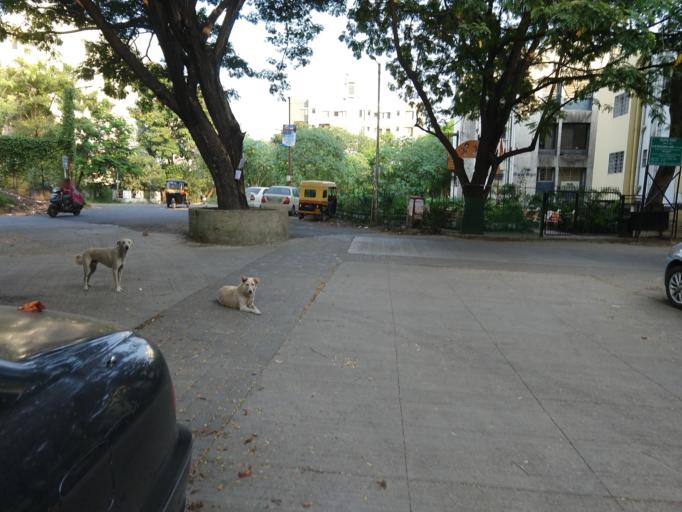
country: IN
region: Maharashtra
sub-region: Pune Division
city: Pune
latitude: 18.5090
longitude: 73.7921
